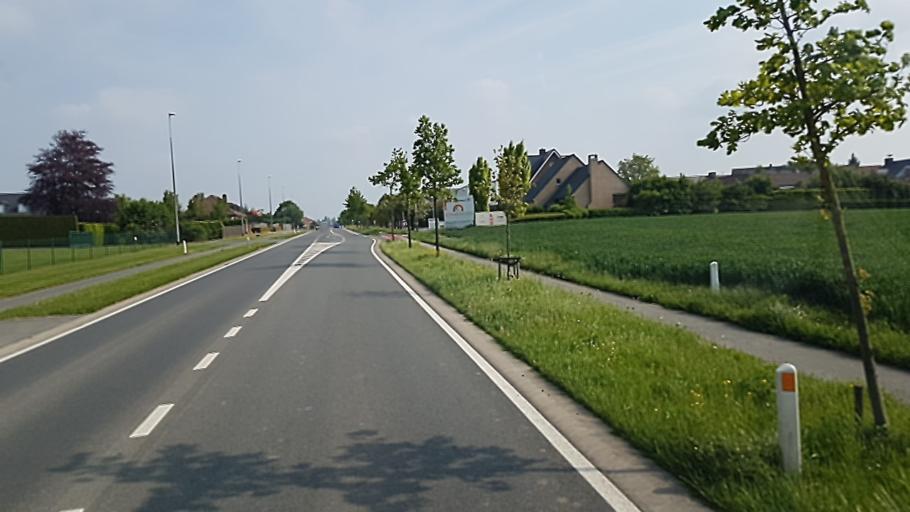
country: BE
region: Flanders
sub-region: Provincie West-Vlaanderen
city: Zwevegem
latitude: 50.7864
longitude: 3.2966
